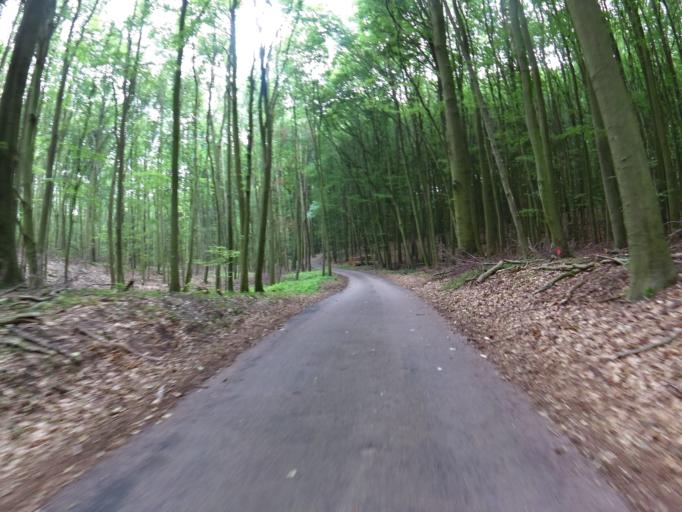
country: DE
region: Mecklenburg-Vorpommern
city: Seebad Heringsdorf
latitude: 53.9018
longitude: 14.1622
